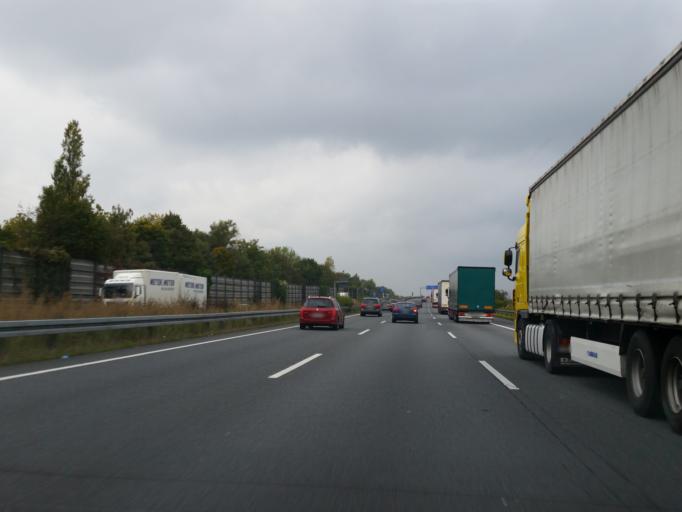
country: DE
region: Lower Saxony
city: Lehrte
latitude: 52.3892
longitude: 9.9844
